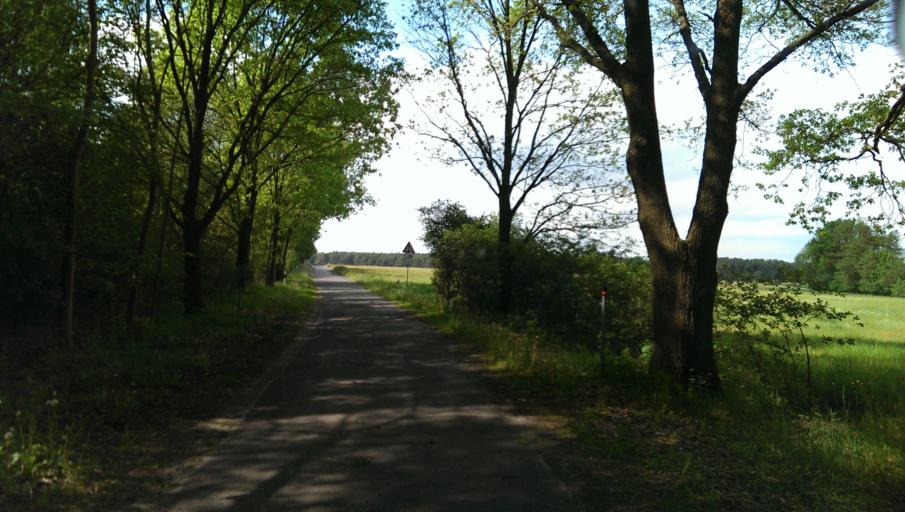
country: DE
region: Brandenburg
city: Linthe
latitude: 52.1519
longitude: 12.7193
